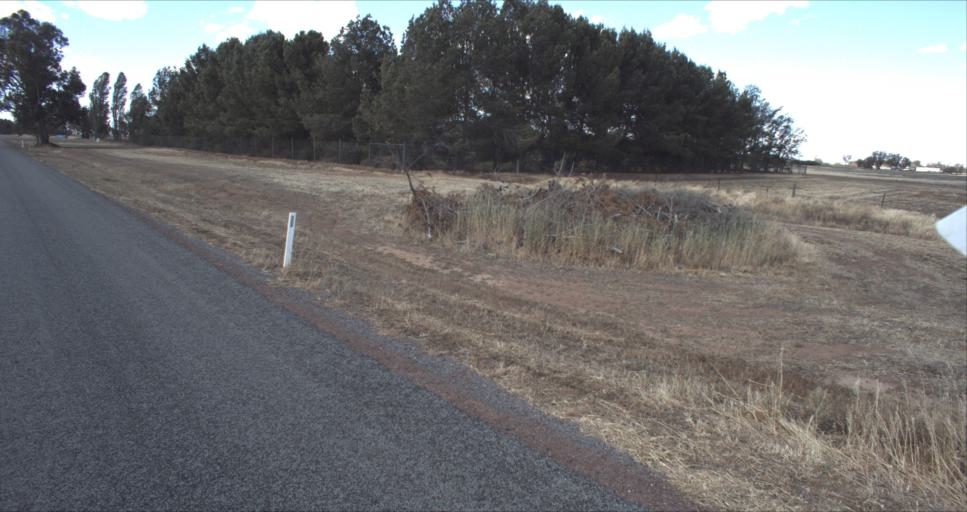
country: AU
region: New South Wales
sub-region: Leeton
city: Leeton
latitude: -34.4858
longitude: 146.2482
